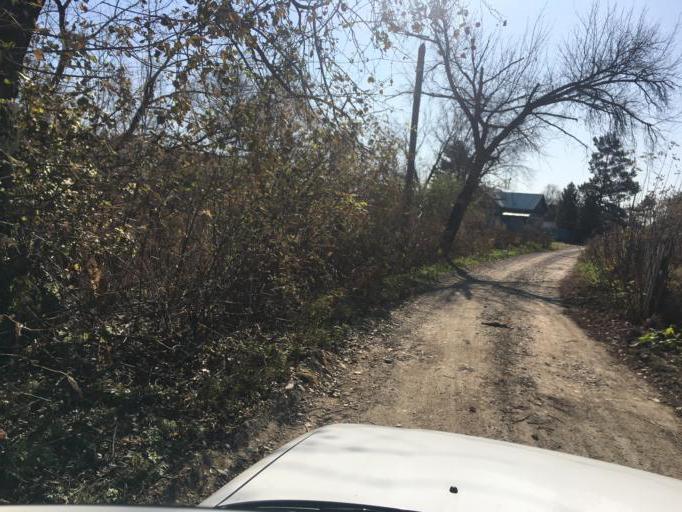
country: RU
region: Primorskiy
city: Dal'nerechensk
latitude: 45.9099
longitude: 133.7953
